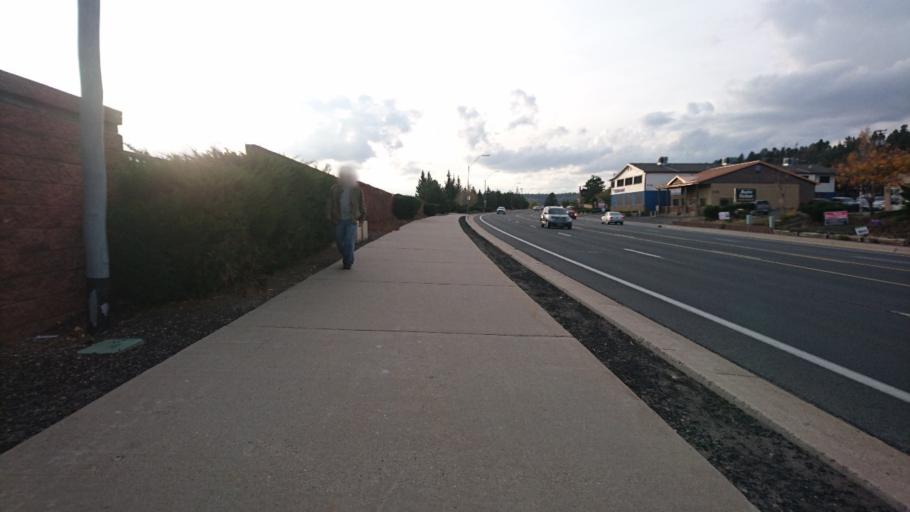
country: US
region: Arizona
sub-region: Coconino County
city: Flagstaff
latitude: 35.1935
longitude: -111.6353
